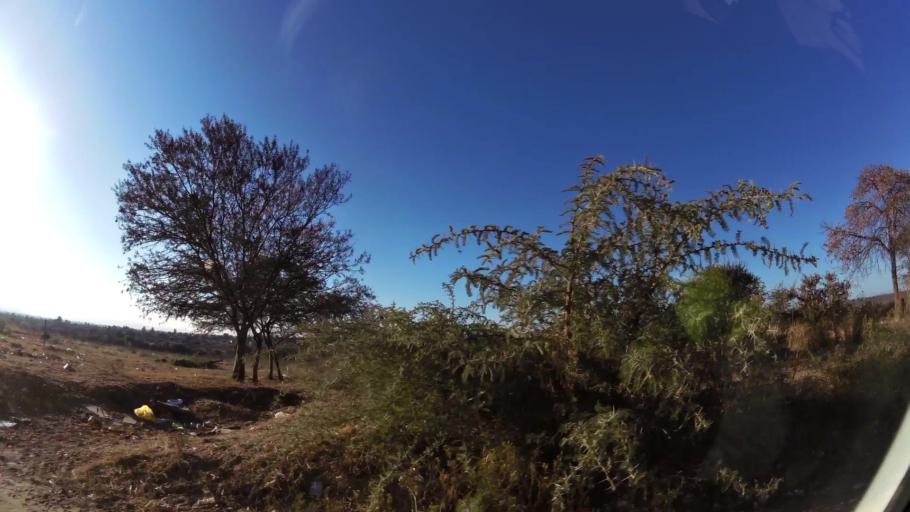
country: ZA
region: Limpopo
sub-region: Capricorn District Municipality
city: Polokwane
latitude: -23.8493
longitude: 29.3562
